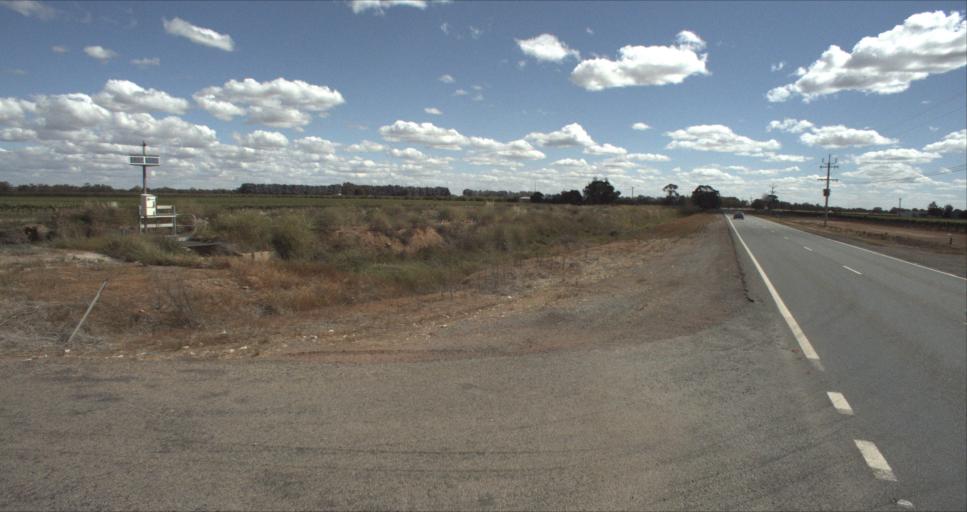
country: AU
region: New South Wales
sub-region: Leeton
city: Leeton
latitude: -34.5051
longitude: 146.2213
